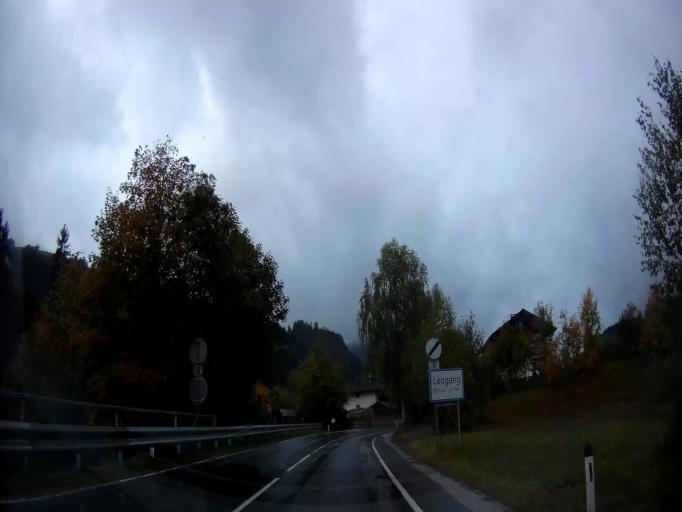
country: AT
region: Salzburg
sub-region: Politischer Bezirk Zell am See
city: Leogang
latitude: 47.4394
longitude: 12.7230
